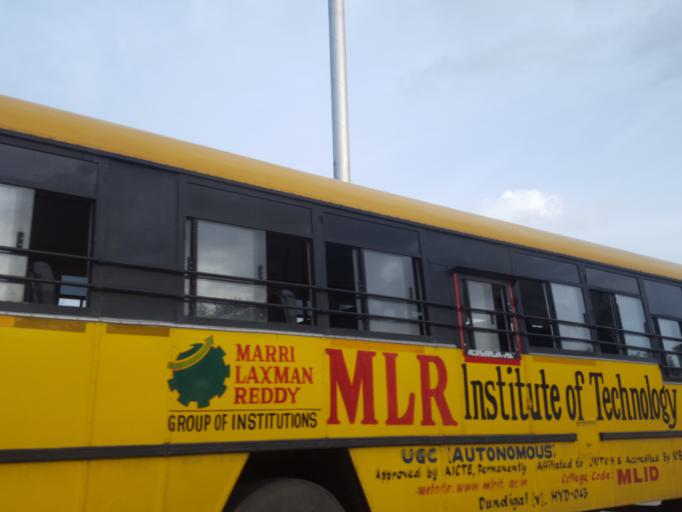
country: IN
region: Telangana
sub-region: Rangareddi
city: Quthbullapur
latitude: 17.5961
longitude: 78.4410
